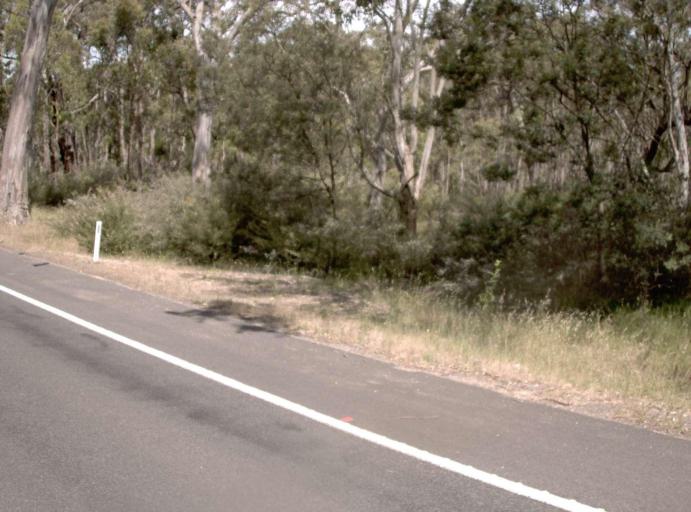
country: AU
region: Victoria
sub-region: Wellington
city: Sale
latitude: -37.9217
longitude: 147.2483
